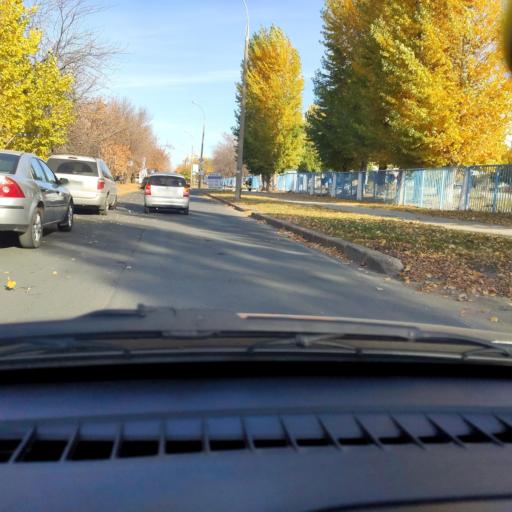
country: RU
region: Samara
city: Tol'yatti
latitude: 53.5222
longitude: 49.3215
